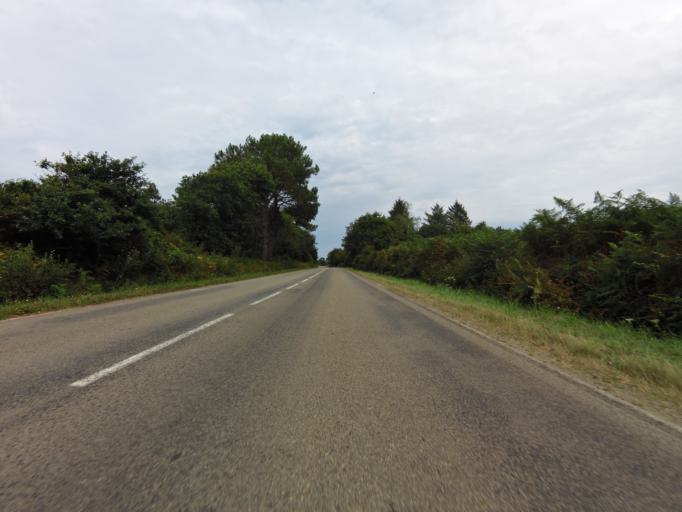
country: FR
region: Brittany
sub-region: Departement du Finistere
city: Poullan-sur-Mer
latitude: 48.0758
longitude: -4.4489
